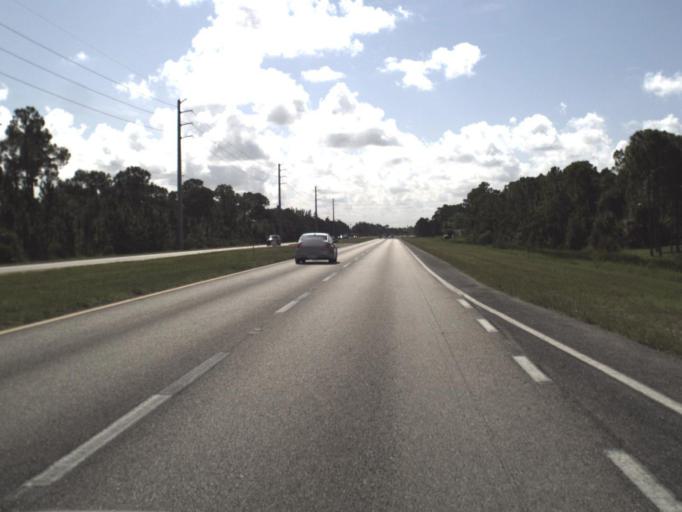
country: US
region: Florida
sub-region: Charlotte County
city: Charlotte Park
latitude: 26.8644
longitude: -81.9952
